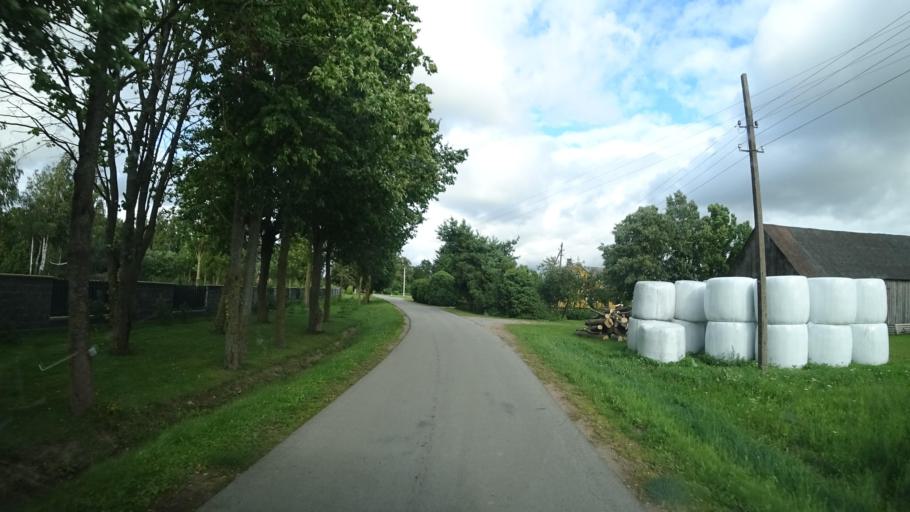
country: LT
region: Marijampoles apskritis
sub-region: Marijampole Municipality
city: Marijampole
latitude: 54.5188
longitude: 23.3327
